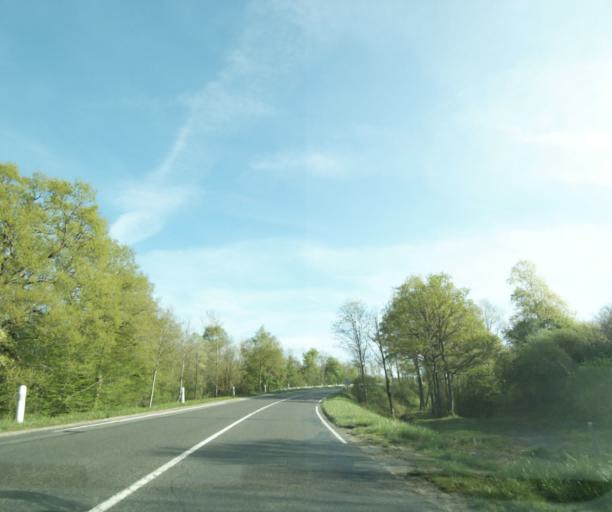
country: FR
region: Ile-de-France
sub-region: Departement de Seine-et-Marne
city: Le Chatelet-en-Brie
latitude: 48.4738
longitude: 2.8650
